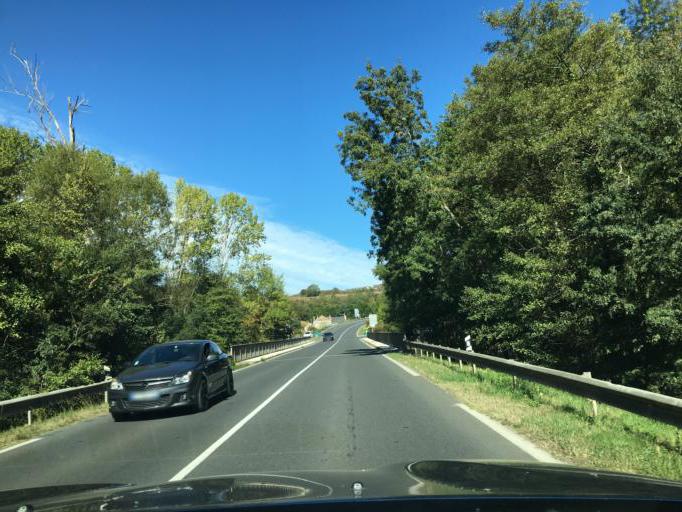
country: FR
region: Centre
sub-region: Departement d'Indre-et-Loire
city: Azay-le-Rideau
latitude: 47.2604
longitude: 0.4574
